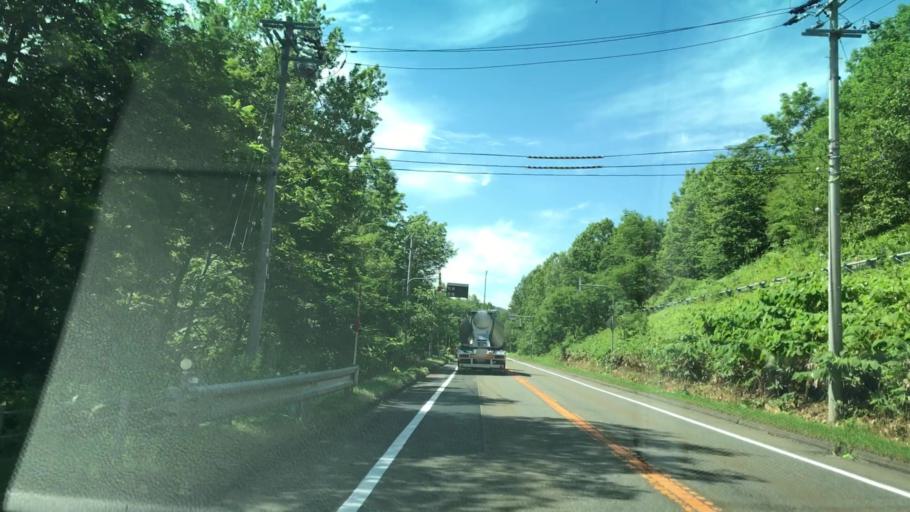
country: JP
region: Hokkaido
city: Shimo-furano
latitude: 42.9111
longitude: 142.4460
